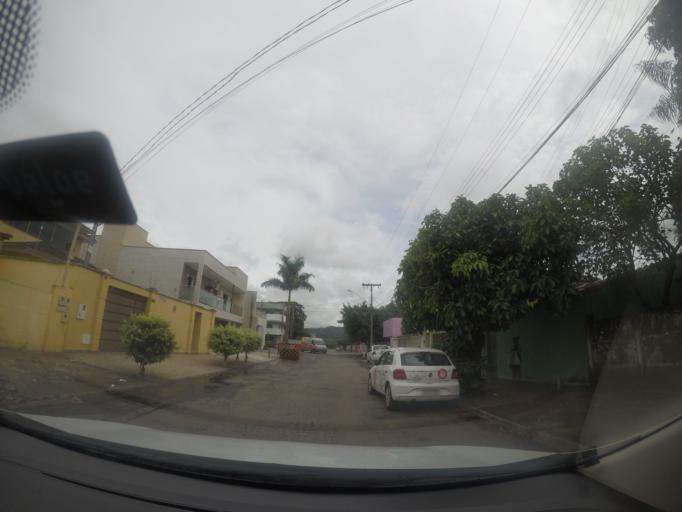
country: BR
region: Goias
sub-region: Goiania
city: Goiania
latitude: -16.6886
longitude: -49.3342
